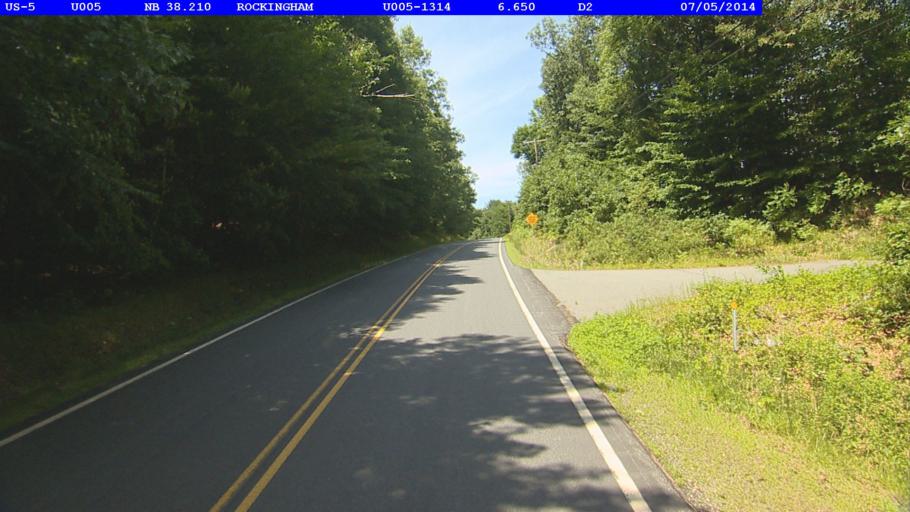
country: US
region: New Hampshire
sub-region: Sullivan County
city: Charlestown
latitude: 43.2106
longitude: -72.4502
